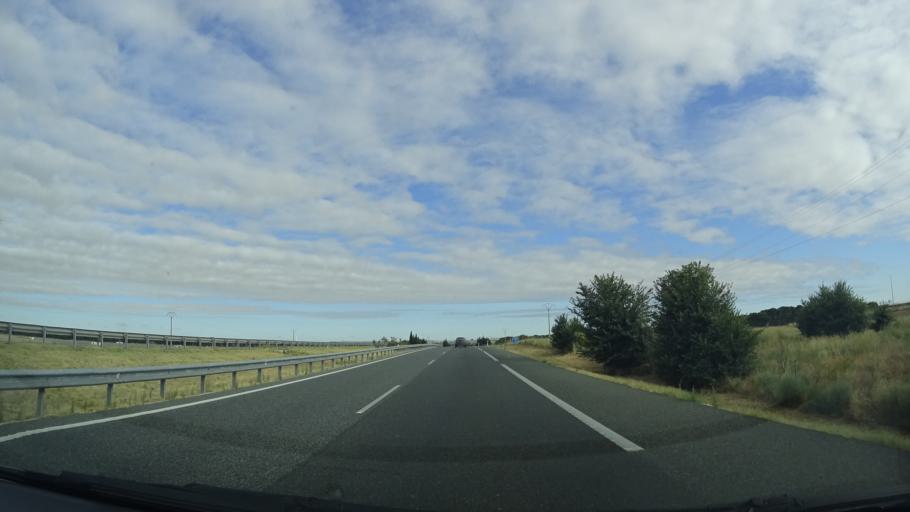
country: ES
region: Castille and Leon
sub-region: Provincia de Valladolid
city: San Vicente del Palacio
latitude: 41.2578
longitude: -4.8757
